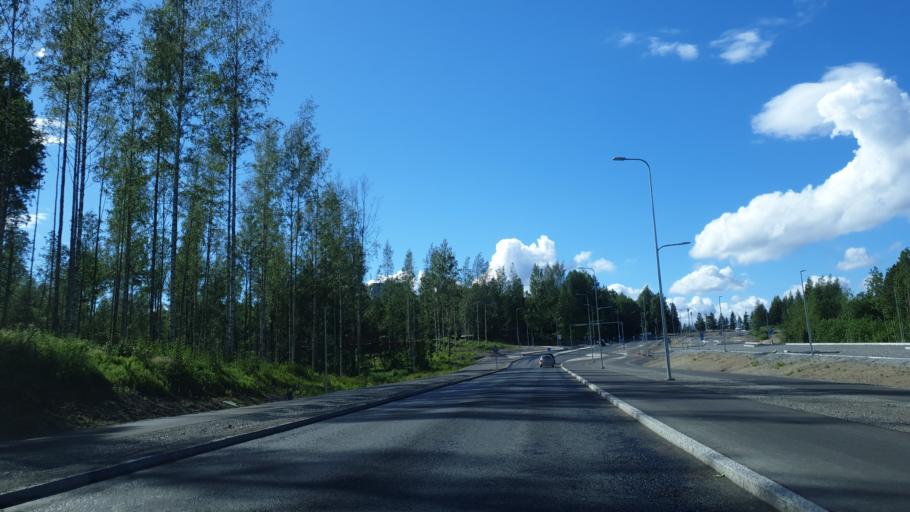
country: FI
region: Northern Savo
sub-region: Kuopio
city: Kuopio
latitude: 62.9039
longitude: 27.6573
